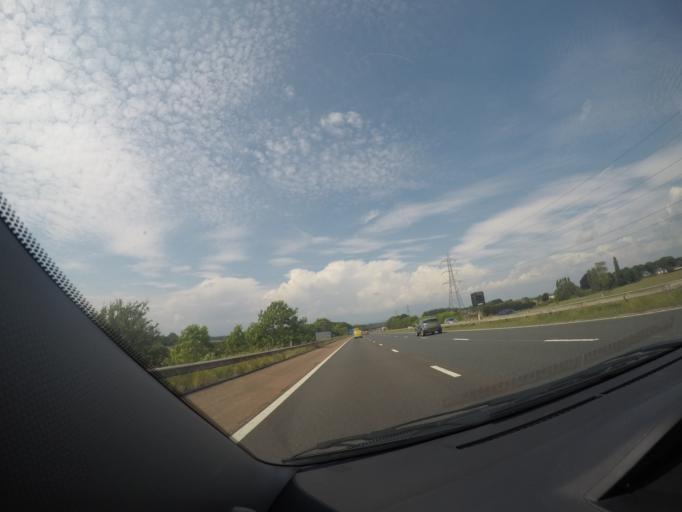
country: GB
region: England
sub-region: Cumbria
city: Scotby
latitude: 54.8883
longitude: -2.8853
